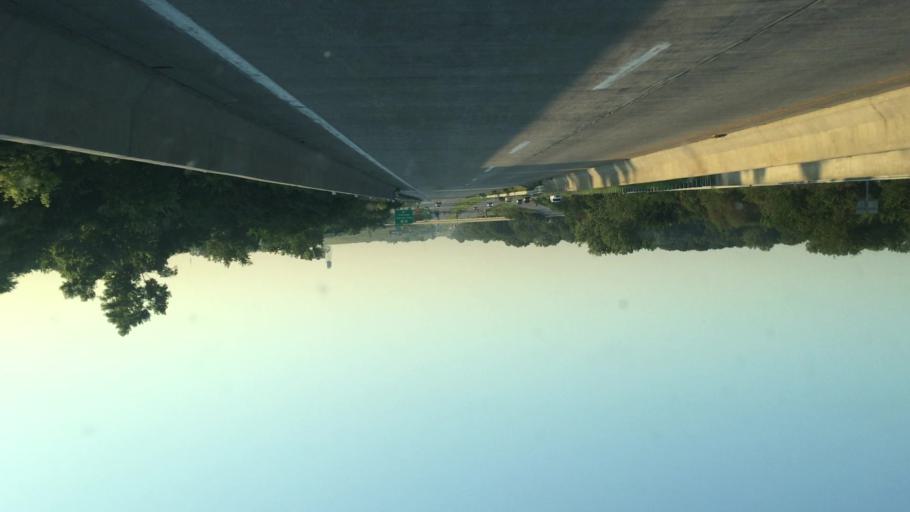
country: US
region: Missouri
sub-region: Platte County
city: Platte City
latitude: 39.5116
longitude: -94.7866
